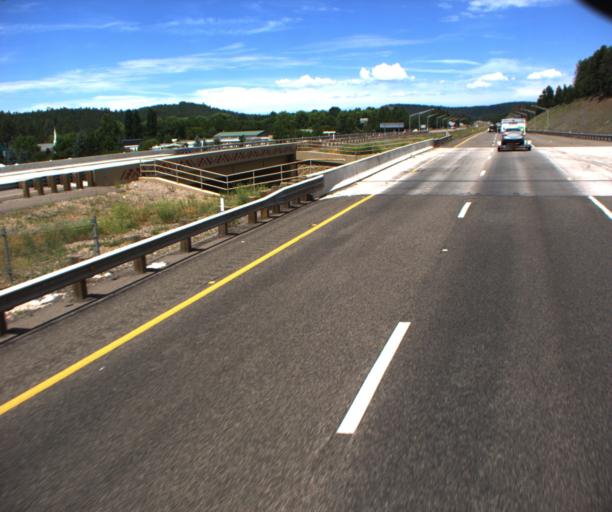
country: US
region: Arizona
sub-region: Coconino County
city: Sedona
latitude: 34.9418
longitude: -111.6530
